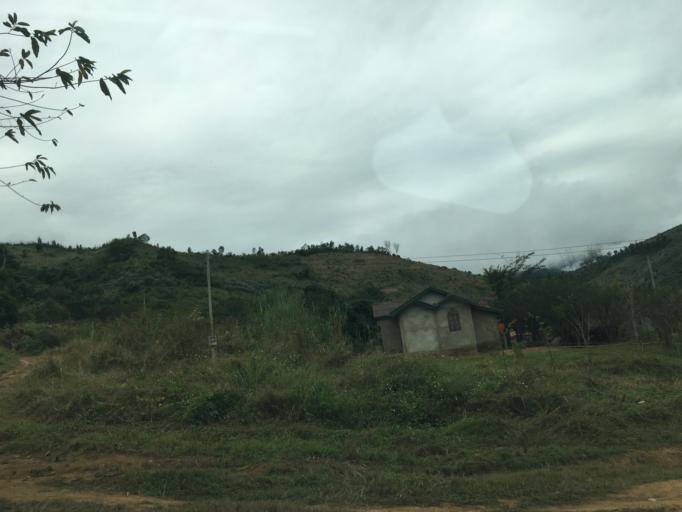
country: LA
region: Houaphan
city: Viengthong
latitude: 19.9399
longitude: 103.2916
